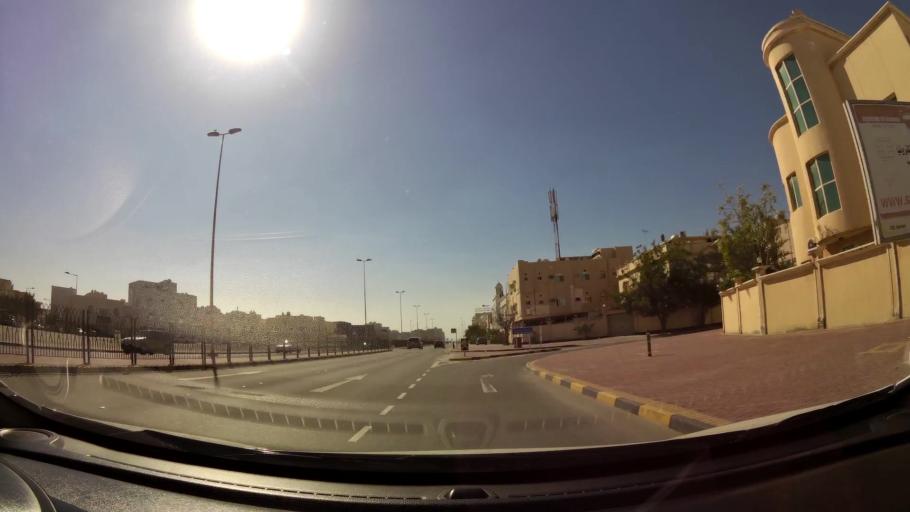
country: BH
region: Muharraq
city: Al Hadd
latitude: 26.2342
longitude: 50.6557
